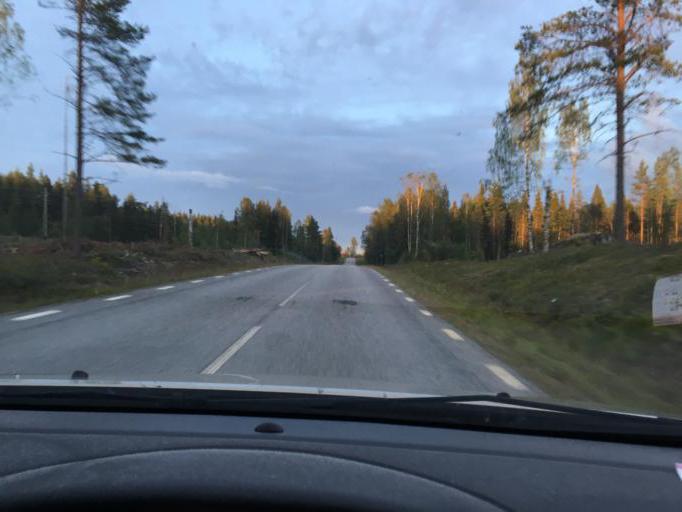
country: SE
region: Norrbotten
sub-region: Lulea Kommun
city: Ranea
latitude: 66.0520
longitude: 22.3845
